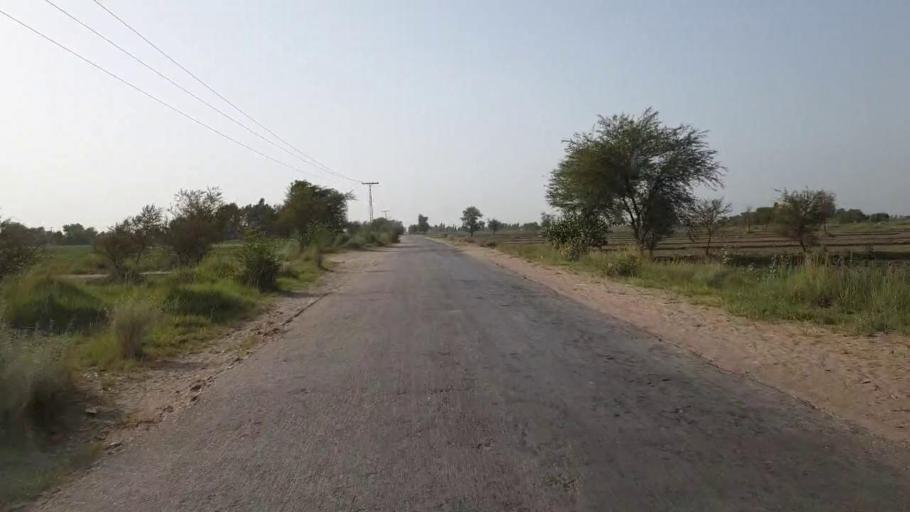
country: PK
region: Sindh
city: Jam Sahib
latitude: 26.3841
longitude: 68.8843
